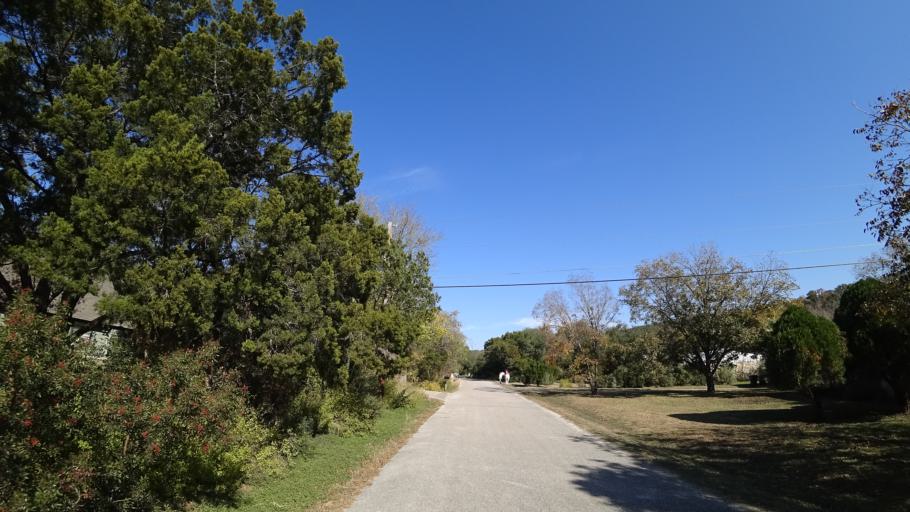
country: US
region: Texas
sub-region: Williamson County
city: Jollyville
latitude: 30.3933
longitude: -97.7791
